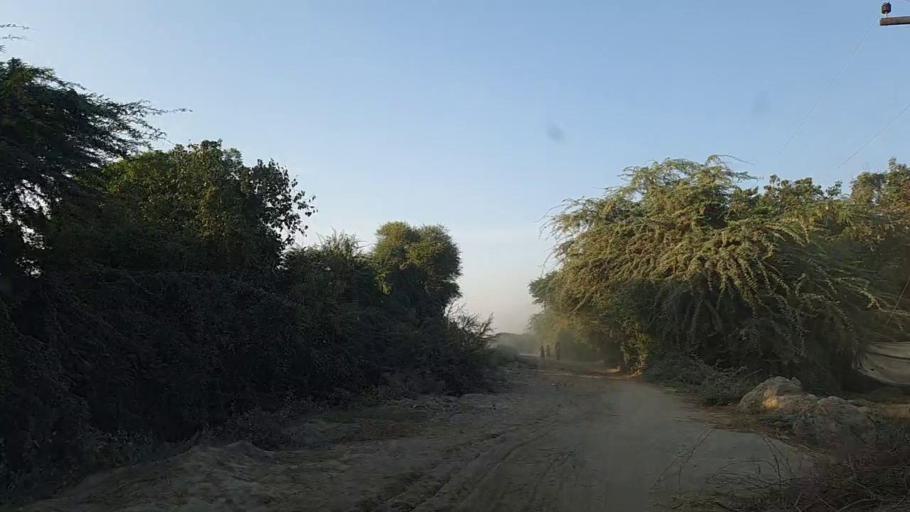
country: PK
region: Sindh
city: Mirpur Batoro
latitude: 24.7070
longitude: 68.2159
